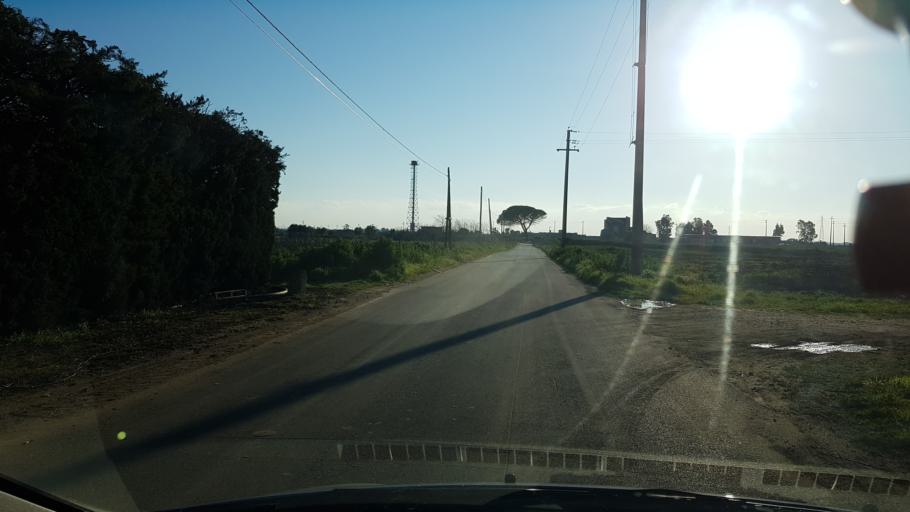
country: IT
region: Apulia
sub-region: Provincia di Brindisi
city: Brindisi
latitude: 40.5922
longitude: 17.8974
